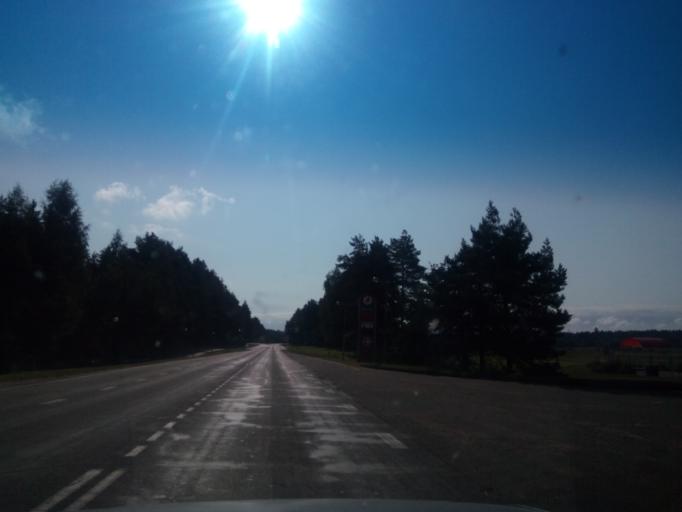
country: BY
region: Vitebsk
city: Vyerkhnyadzvinsk
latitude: 55.7571
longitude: 27.9525
